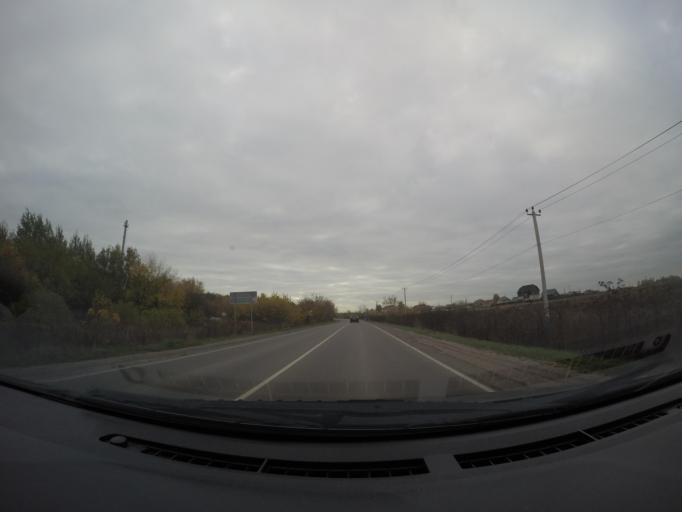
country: RU
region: Moskovskaya
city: Elektrougli
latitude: 55.7681
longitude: 38.2038
